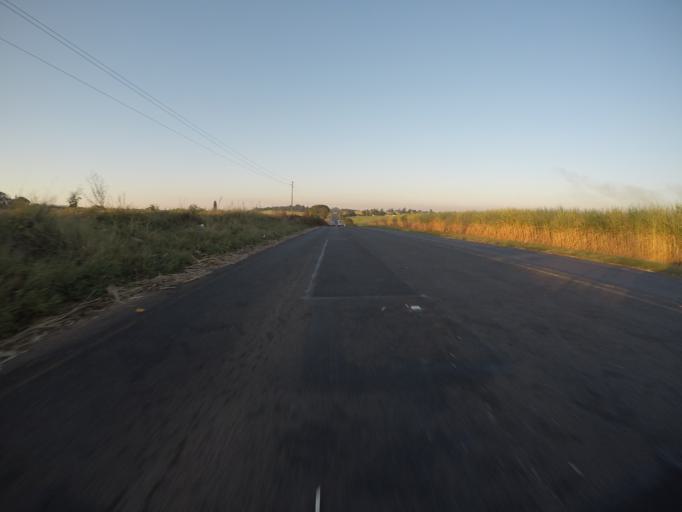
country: ZA
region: KwaZulu-Natal
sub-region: uThungulu District Municipality
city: Empangeni
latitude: -28.7846
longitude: 31.8974
